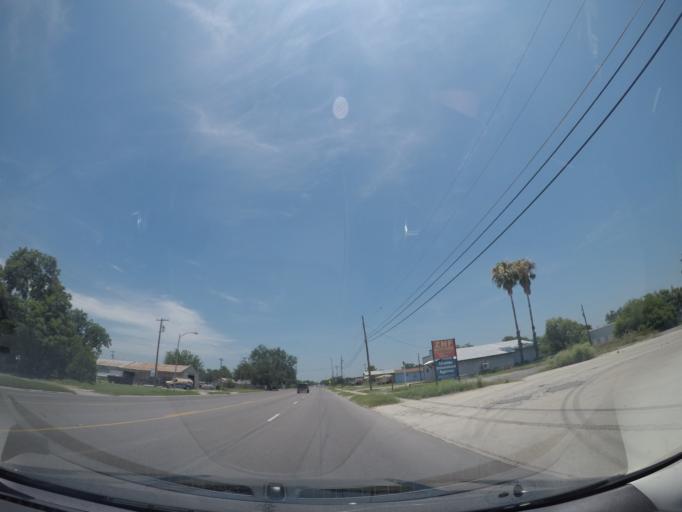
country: US
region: Texas
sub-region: Uvalde County
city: Uvalde
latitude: 29.2016
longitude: -99.8068
